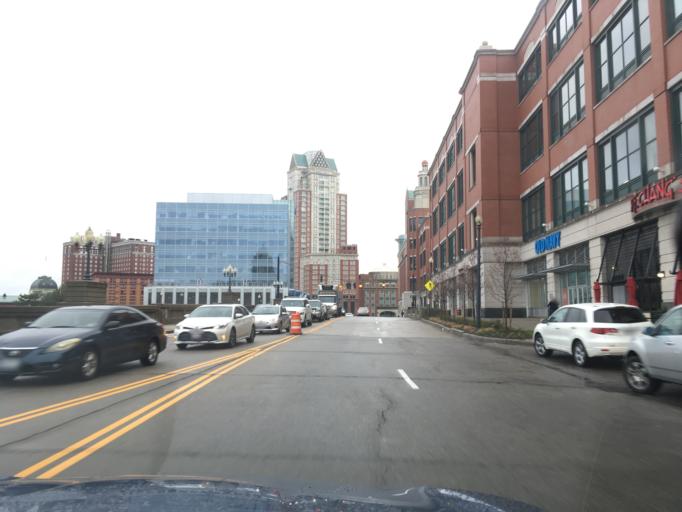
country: US
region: Rhode Island
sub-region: Providence County
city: Providence
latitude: 41.8285
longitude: -71.4154
